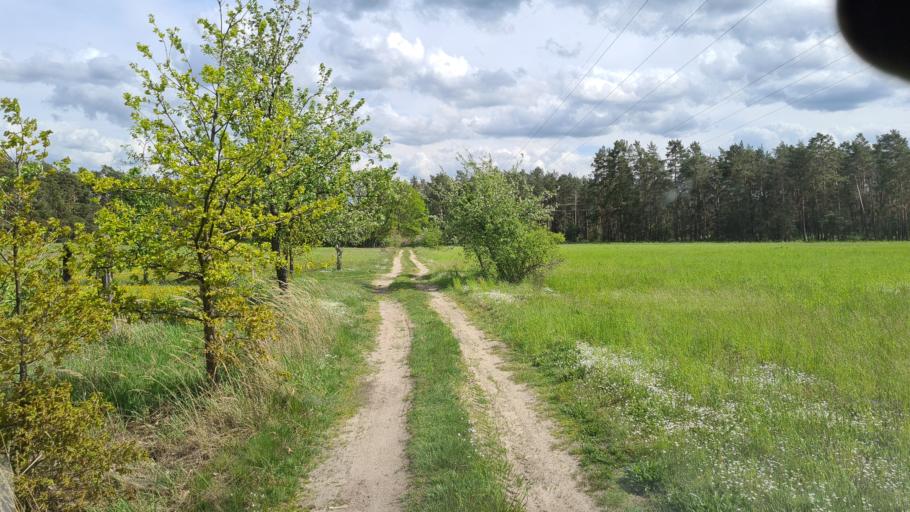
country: DE
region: Brandenburg
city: Crinitz
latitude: 51.7158
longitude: 13.7753
